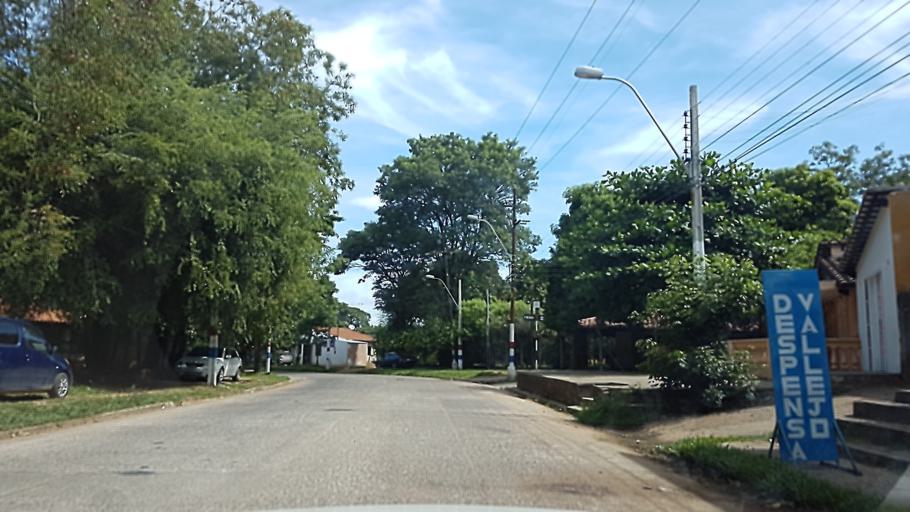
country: PY
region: Central
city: Colonia Mariano Roque Alonso
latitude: -25.1973
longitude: -57.5354
